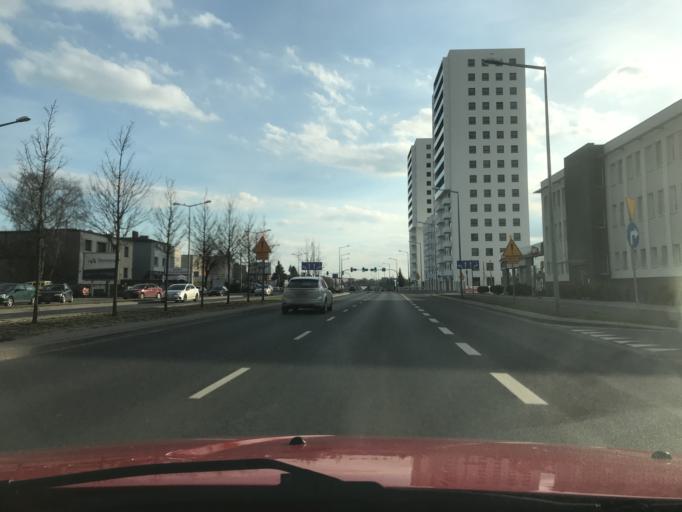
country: PL
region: Greater Poland Voivodeship
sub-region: Powiat poznanski
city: Lubon
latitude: 52.4029
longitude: 16.8658
